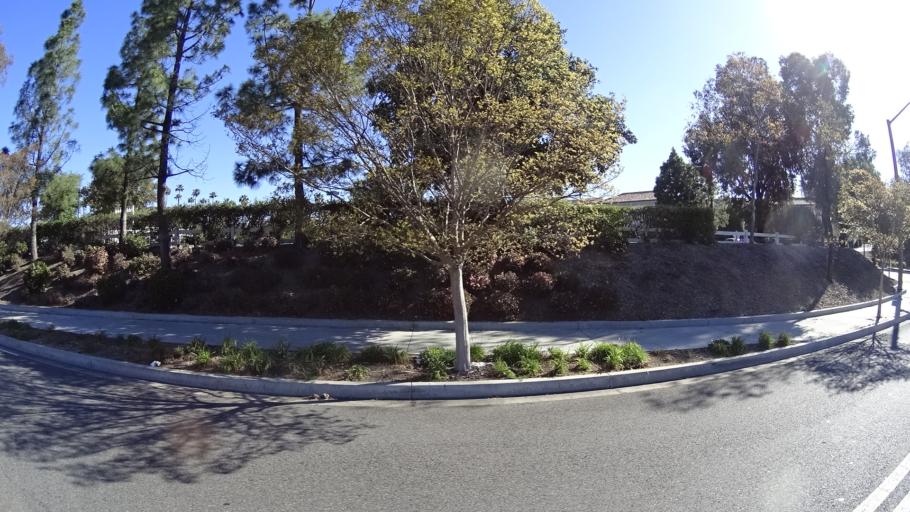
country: US
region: California
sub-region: Ventura County
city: Casa Conejo
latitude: 34.1902
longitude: -118.9354
